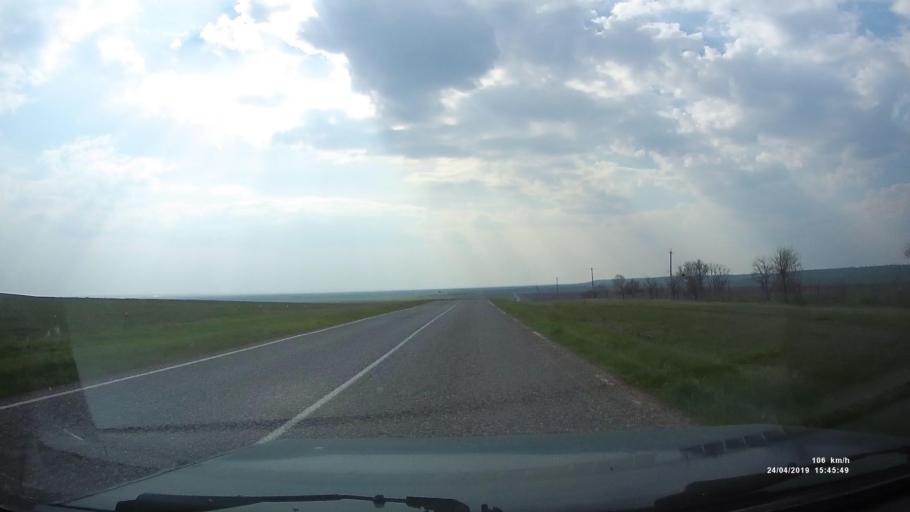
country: RU
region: Kalmykiya
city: Yashalta
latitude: 46.5919
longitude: 42.7288
